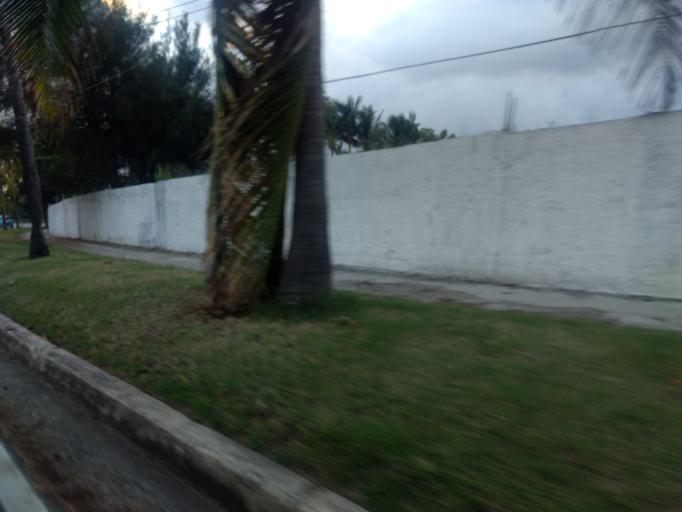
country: CU
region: La Habana
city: Cerro
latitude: 23.0882
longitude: -82.4783
